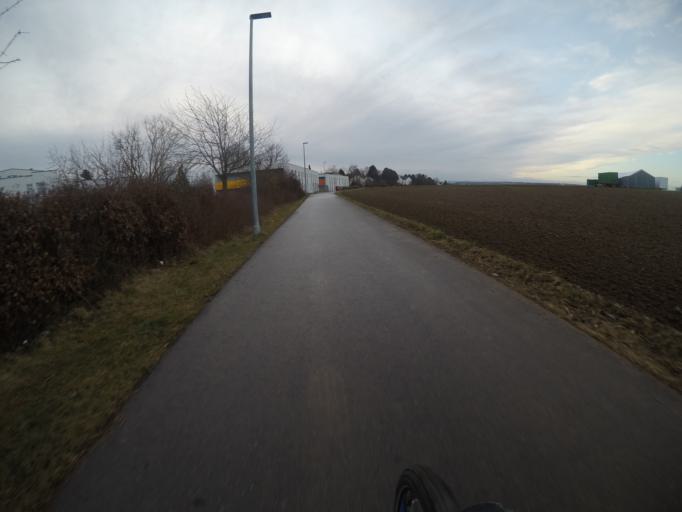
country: DE
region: Baden-Wuerttemberg
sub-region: Regierungsbezirk Stuttgart
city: Ostfildern
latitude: 48.7231
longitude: 9.2044
